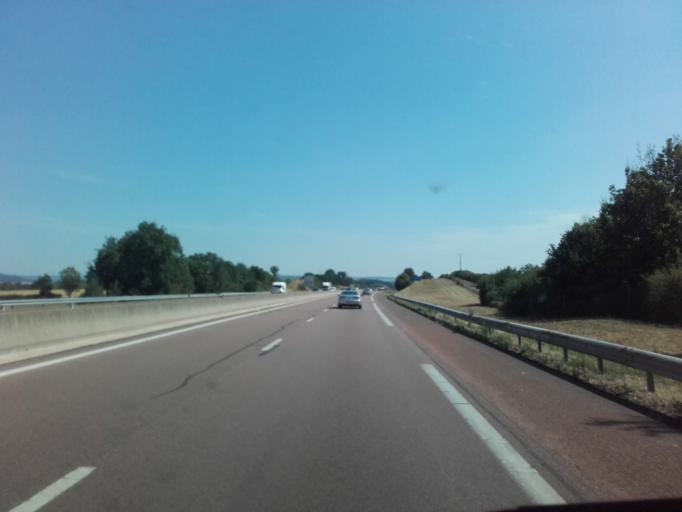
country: FR
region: Bourgogne
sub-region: Departement de la Cote-d'Or
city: Pouilly-en-Auxois
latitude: 47.2414
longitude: 4.5778
